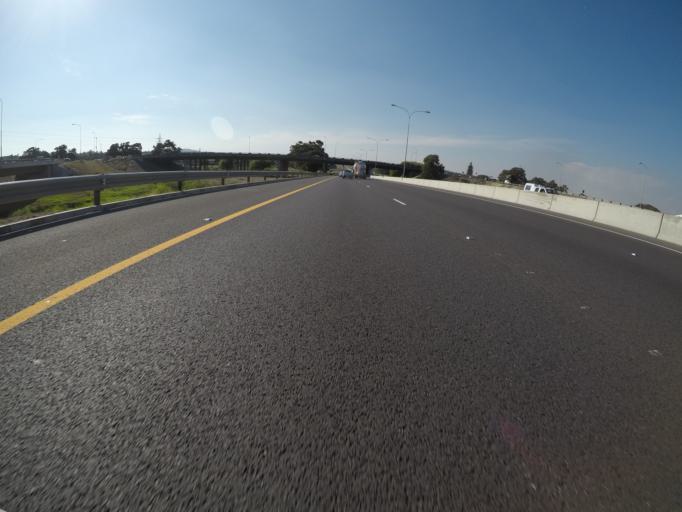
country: ZA
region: Western Cape
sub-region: City of Cape Town
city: Kraaifontein
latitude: -33.8877
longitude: 18.6756
